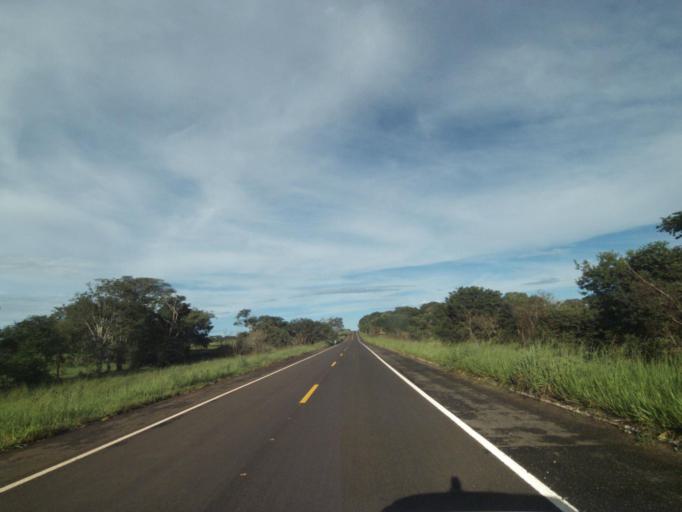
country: BR
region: Goias
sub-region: Itaberai
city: Itaberai
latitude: -15.9108
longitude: -49.5803
